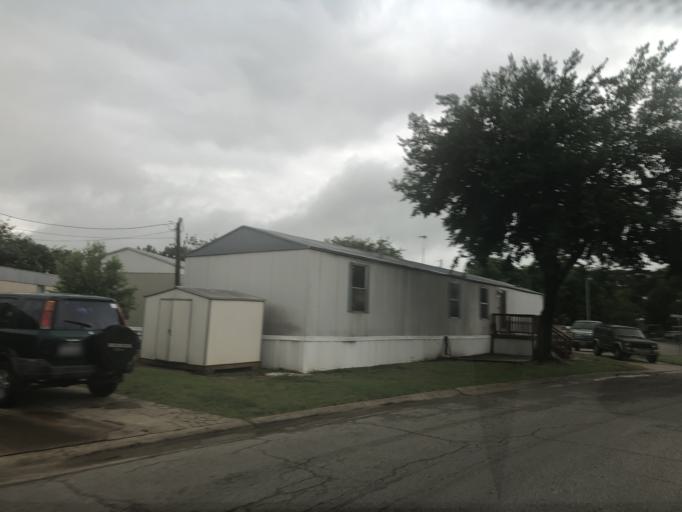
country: US
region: Texas
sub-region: Dallas County
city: Irving
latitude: 32.7933
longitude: -96.9561
